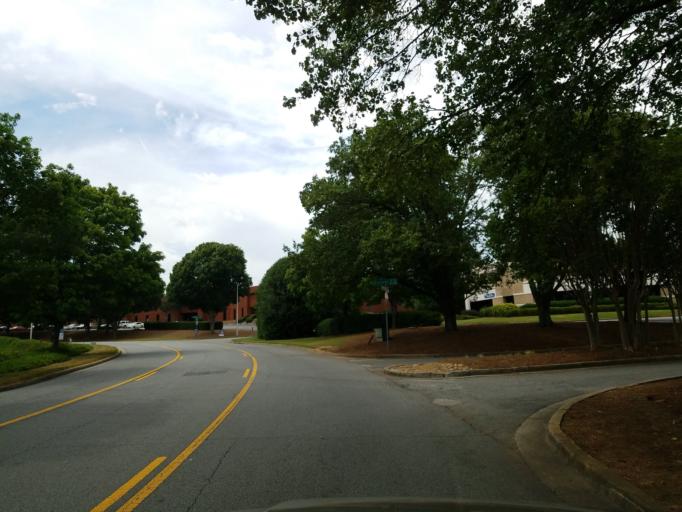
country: US
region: Georgia
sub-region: Cobb County
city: Smyrna
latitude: 33.9196
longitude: -84.4868
